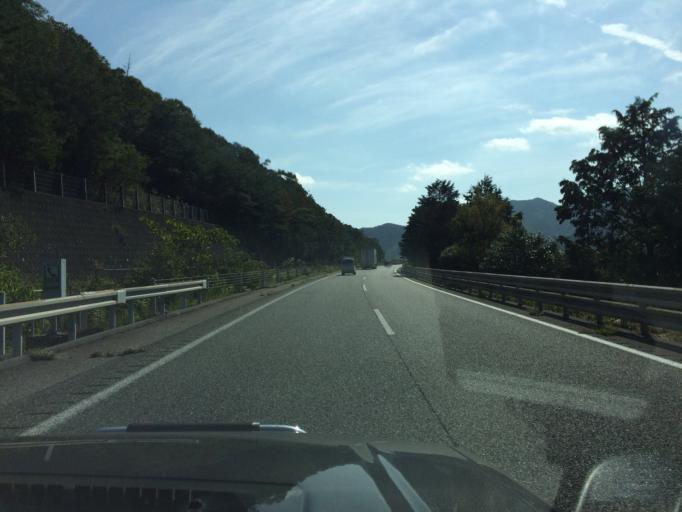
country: JP
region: Hyogo
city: Sasayama
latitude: 35.0110
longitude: 135.1619
